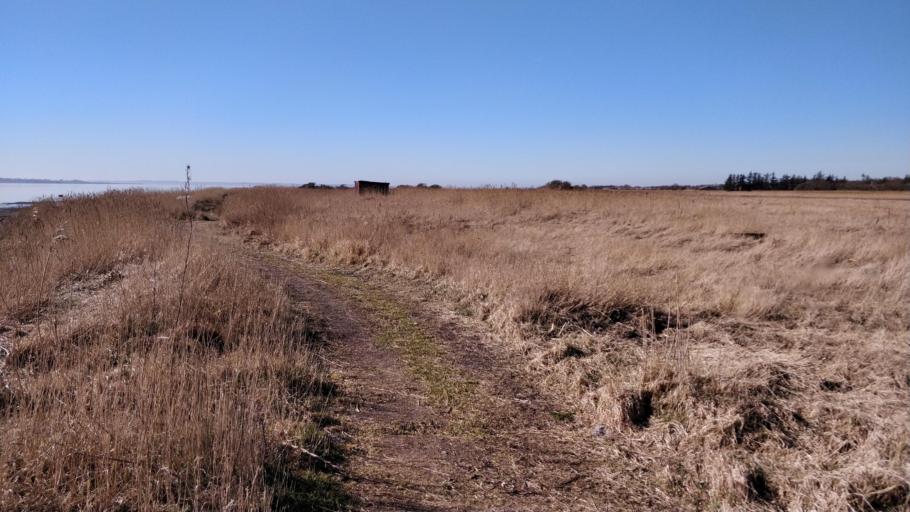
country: DK
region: North Denmark
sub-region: Alborg Kommune
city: Frejlev
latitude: 57.0675
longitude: 9.7494
